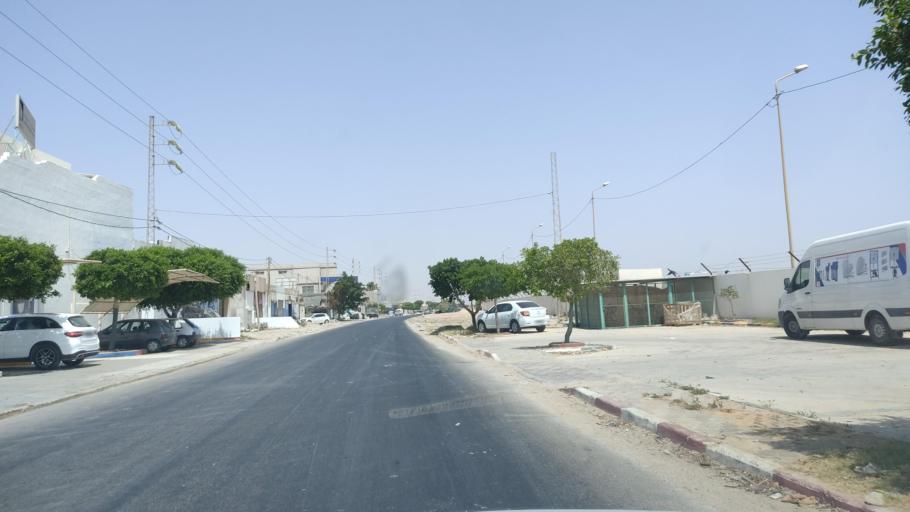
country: TN
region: Safaqis
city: Sfax
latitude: 34.6945
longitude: 10.7243
